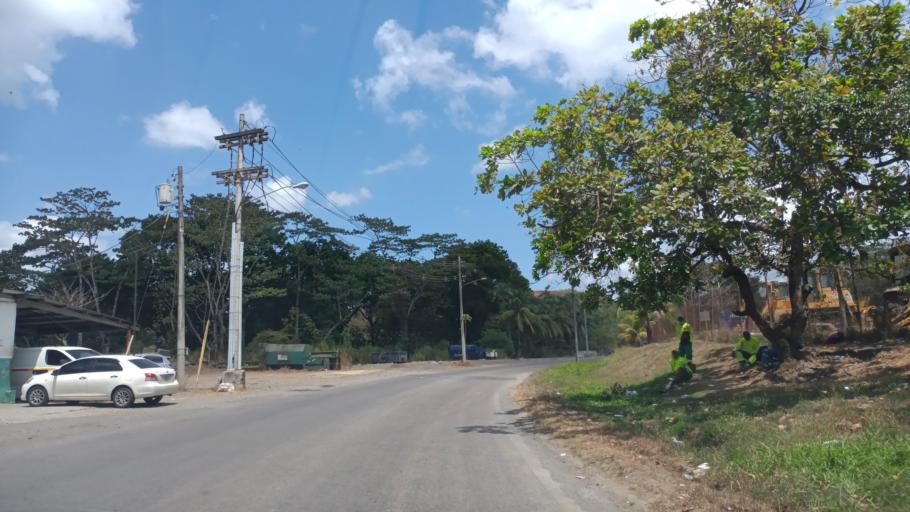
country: PA
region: Panama
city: Las Cumbres
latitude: 9.0455
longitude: -79.5640
